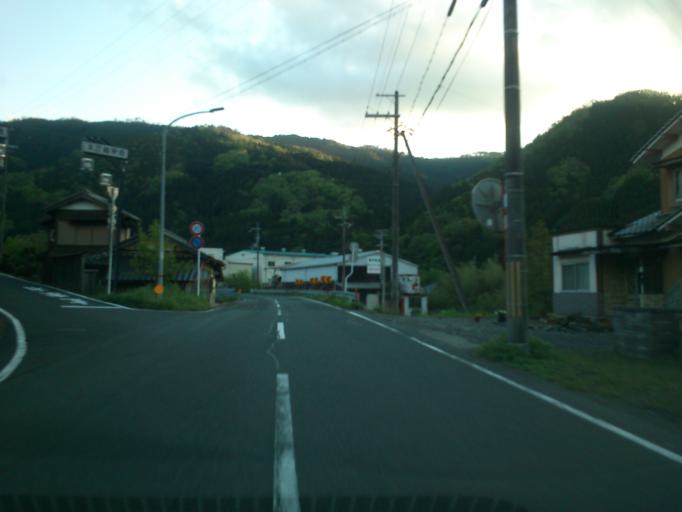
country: JP
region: Kyoto
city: Ayabe
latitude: 35.2628
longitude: 135.3972
